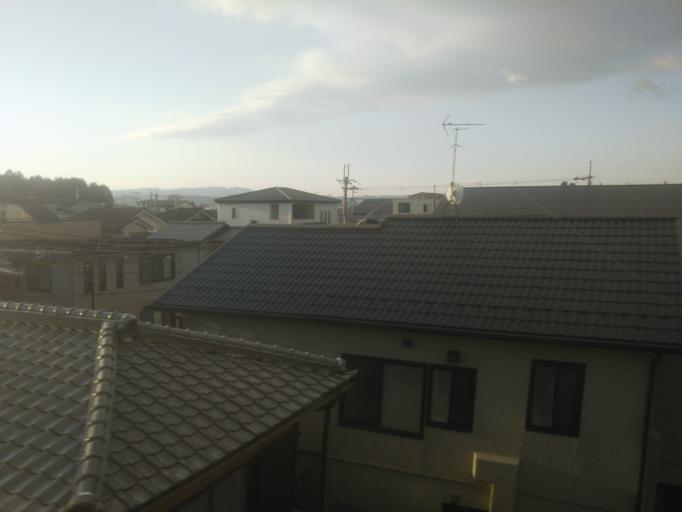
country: JP
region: Shiga Prefecture
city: Kusatsu
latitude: 35.0311
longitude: 135.9749
